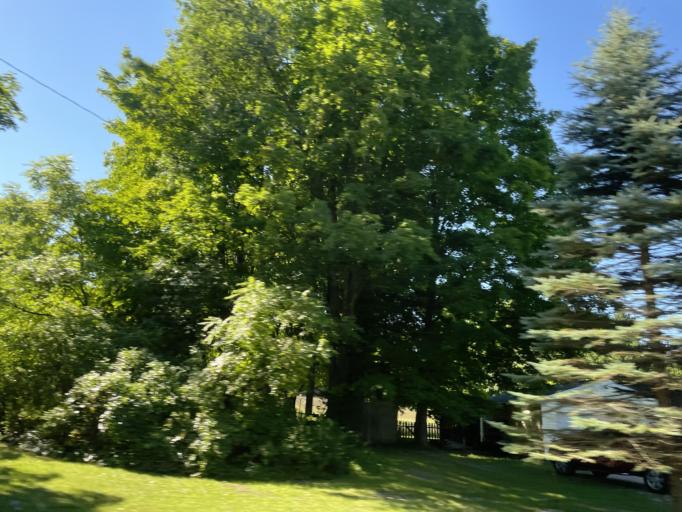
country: US
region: Michigan
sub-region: Benzie County
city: Beulah
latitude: 44.6174
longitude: -86.0812
